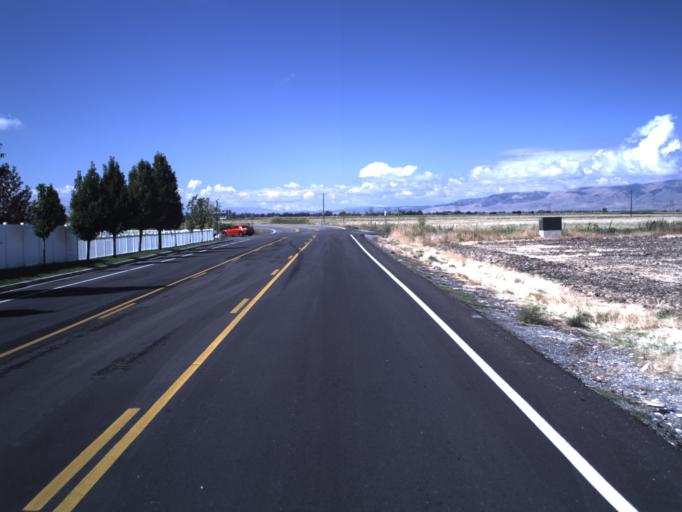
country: US
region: Utah
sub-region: Utah County
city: Springville
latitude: 40.1613
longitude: -111.6557
